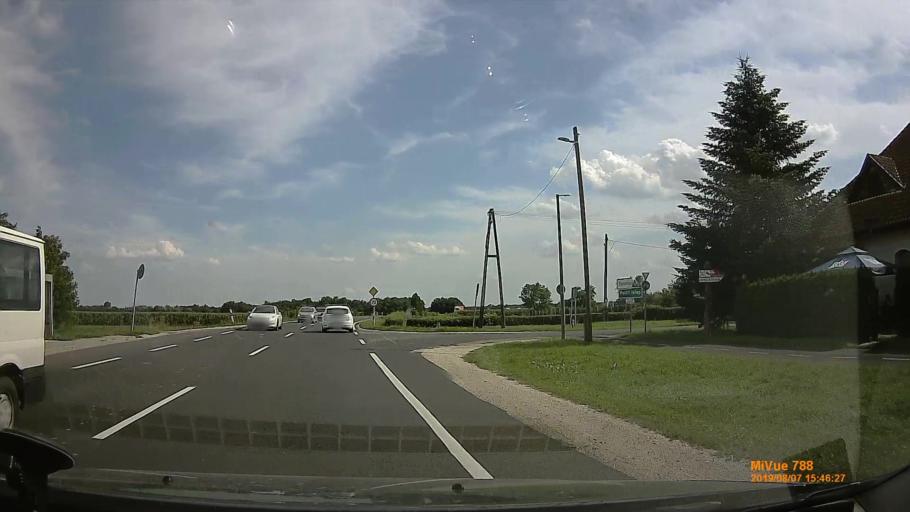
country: HU
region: Vas
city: Szombathely
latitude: 47.1850
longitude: 16.6213
